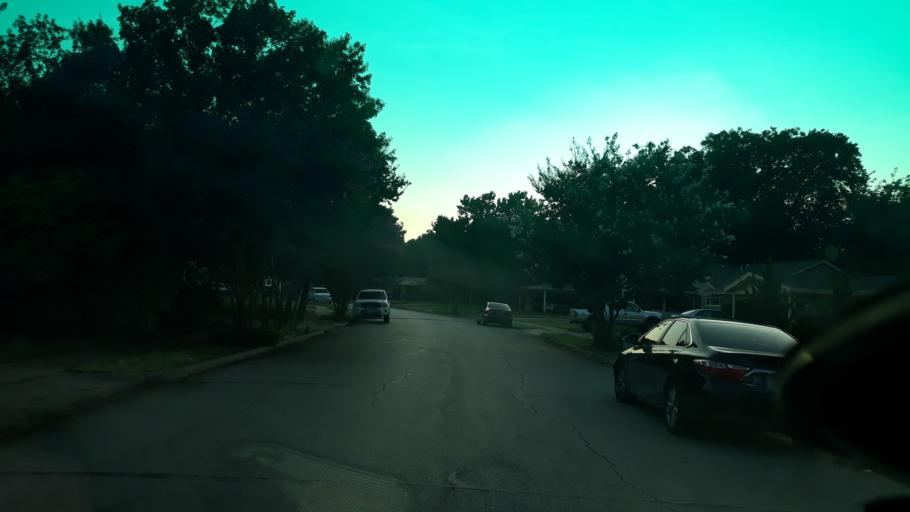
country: US
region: Texas
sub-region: Dallas County
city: Irving
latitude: 32.8335
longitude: -96.9782
